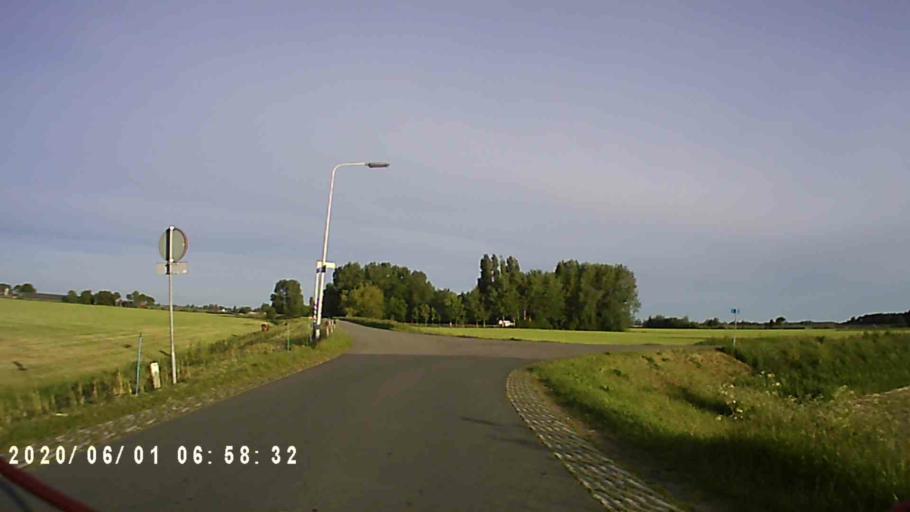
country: NL
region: Friesland
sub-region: Gemeente Dongeradeel
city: Anjum
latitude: 53.3197
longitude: 6.1001
